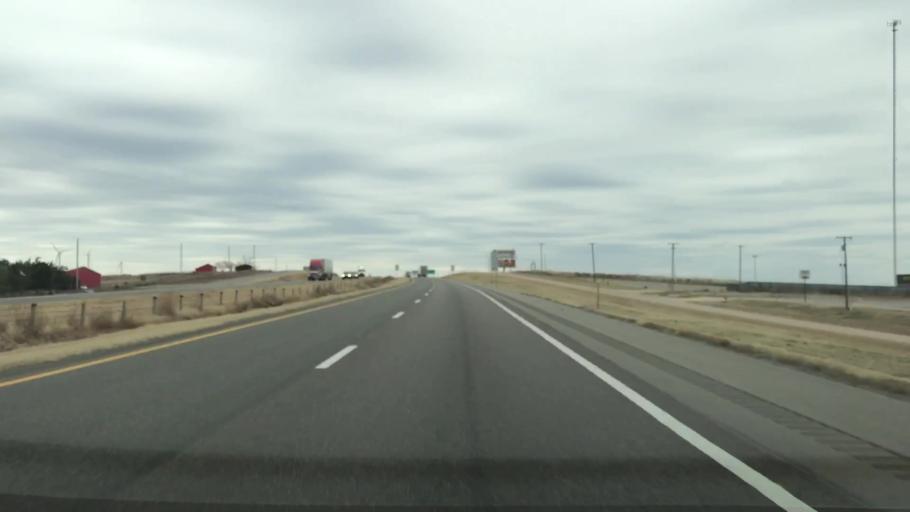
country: US
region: Oklahoma
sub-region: Custer County
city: Weatherford
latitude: 35.5219
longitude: -98.7362
